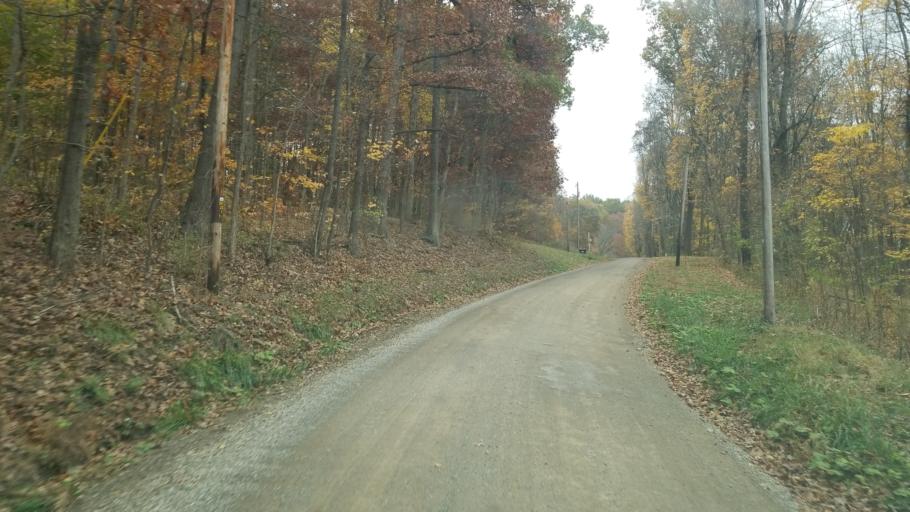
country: US
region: Ohio
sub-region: Licking County
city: Utica
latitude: 40.1678
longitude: -82.3538
